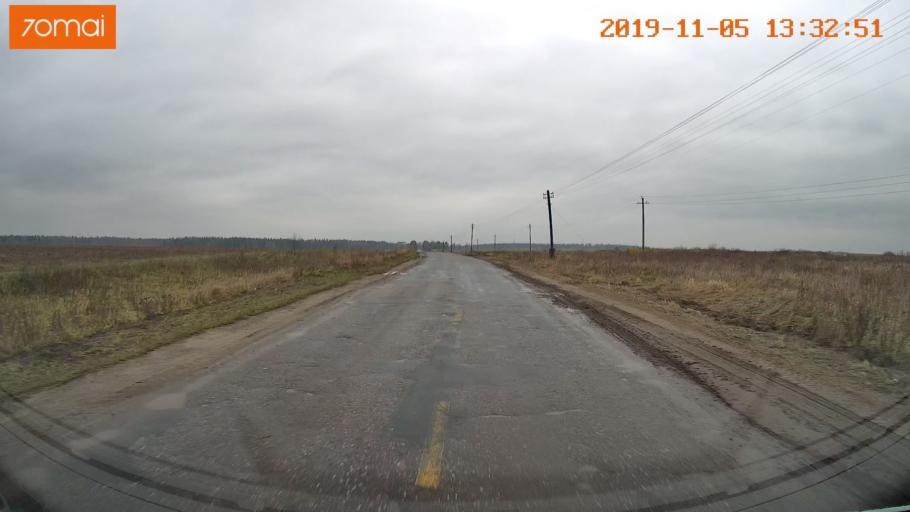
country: RU
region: Ivanovo
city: Shuya
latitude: 56.8868
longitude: 41.3964
